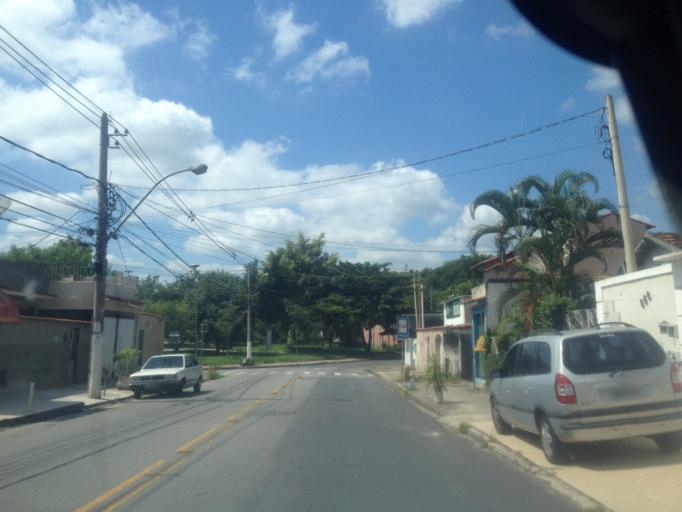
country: BR
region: Rio de Janeiro
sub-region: Volta Redonda
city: Volta Redonda
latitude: -22.5409
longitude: -44.0761
